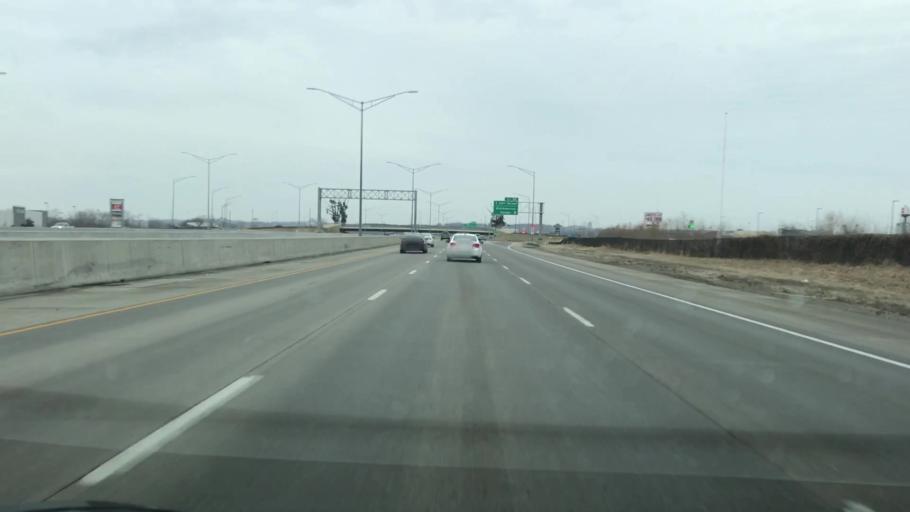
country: US
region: Iowa
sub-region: Pottawattamie County
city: Council Bluffs
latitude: 41.2327
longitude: -95.8722
